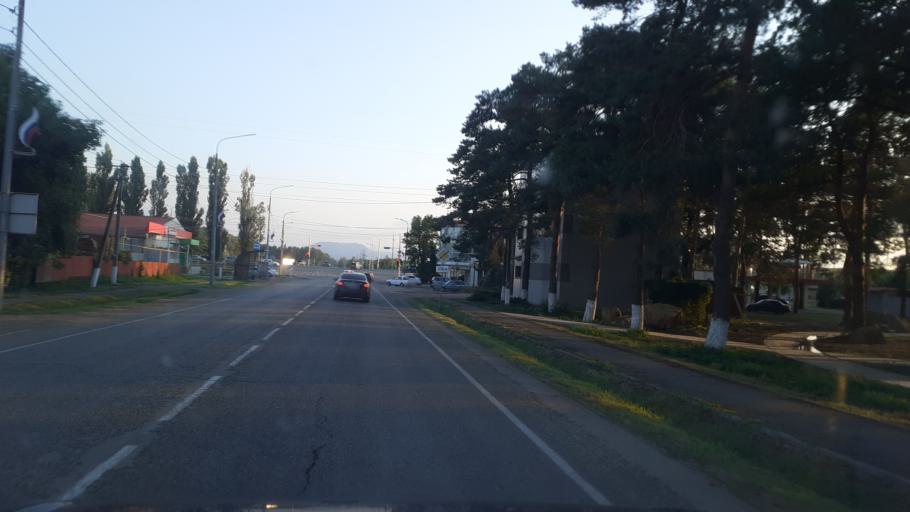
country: RU
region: Krasnodarskiy
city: Severskaya
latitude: 44.8342
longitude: 38.6654
